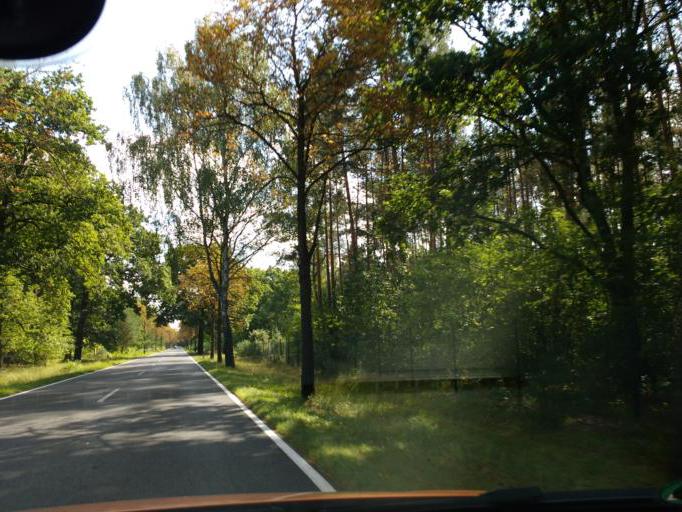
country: DE
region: Brandenburg
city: Oranienburg
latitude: 52.7398
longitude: 13.2757
